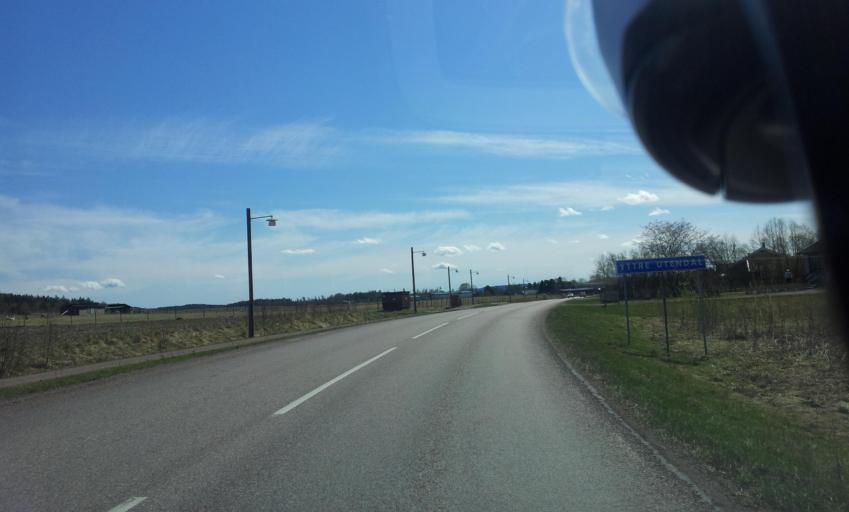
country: SE
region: Dalarna
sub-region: Borlange Kommun
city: Ornas
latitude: 60.4702
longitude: 15.5103
